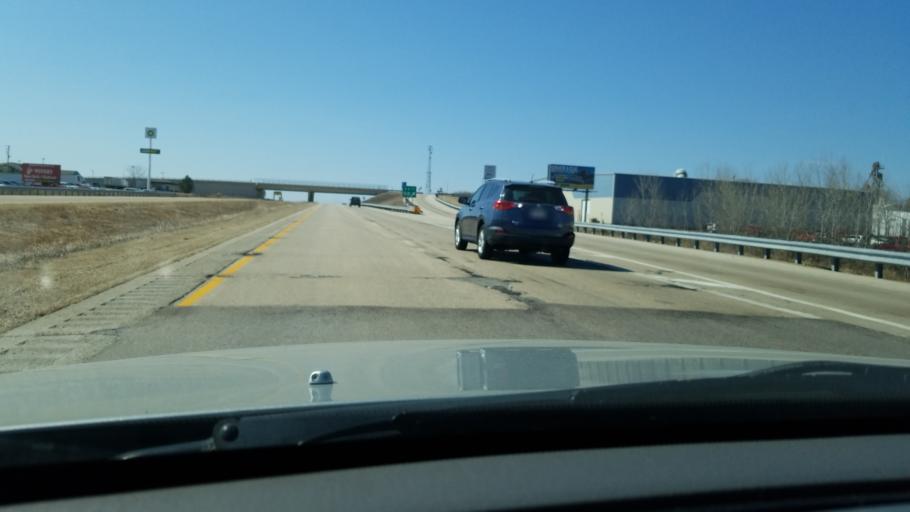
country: US
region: Wisconsin
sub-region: Iowa County
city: Barneveld
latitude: 43.0100
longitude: -89.8979
